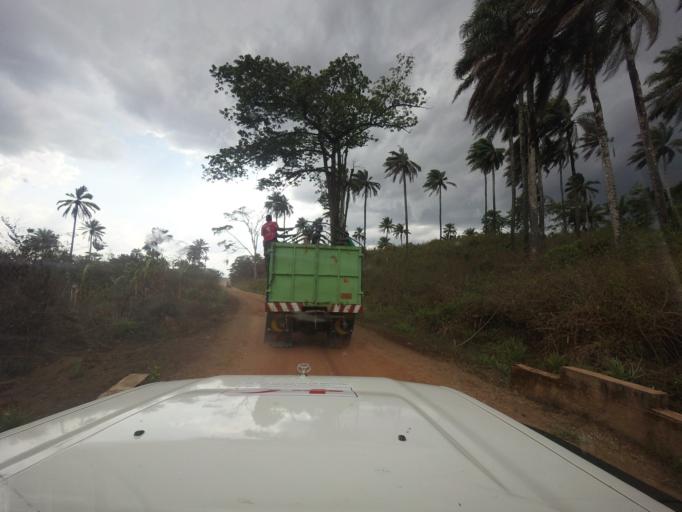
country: LR
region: Lofa
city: Voinjama
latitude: 8.4145
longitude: -9.7224
